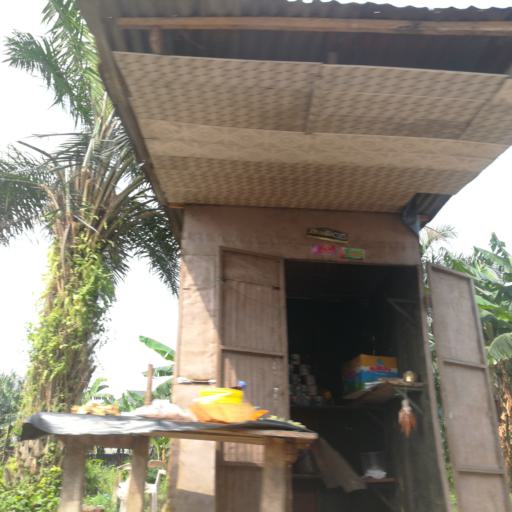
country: NG
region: Rivers
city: Port Harcourt
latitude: 4.8389
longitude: 7.0625
